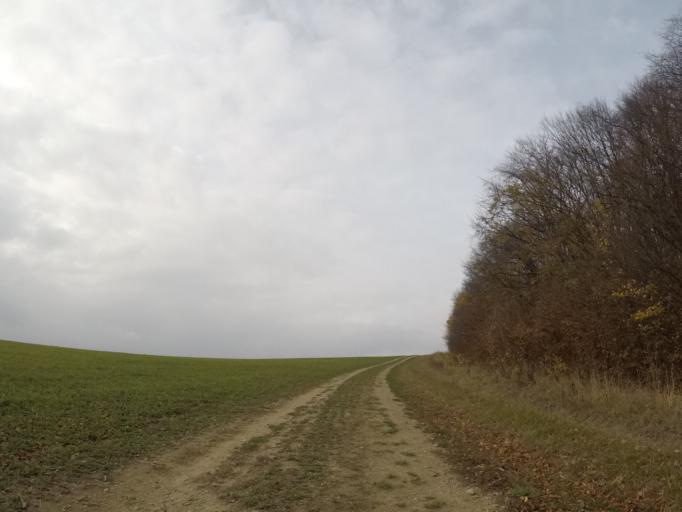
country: SK
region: Presovsky
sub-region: Okres Presov
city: Presov
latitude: 48.9300
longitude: 21.1335
